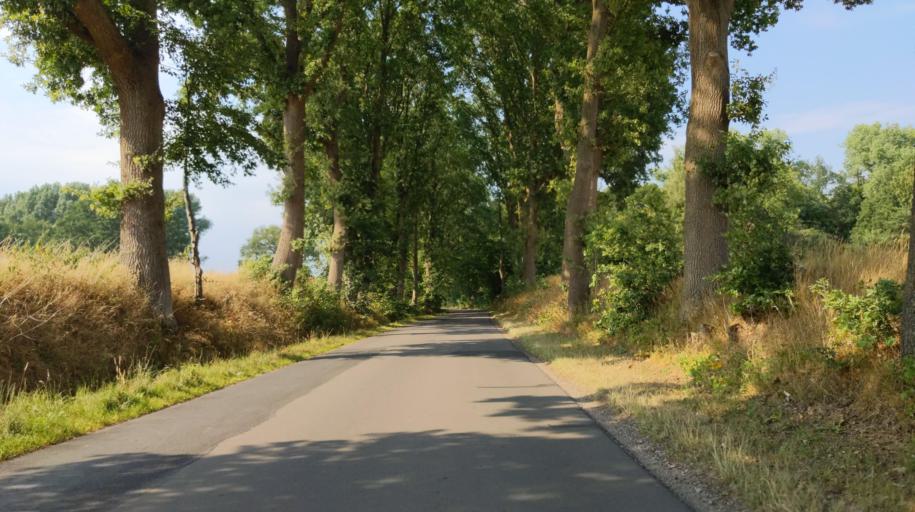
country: DE
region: Schleswig-Holstein
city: Rondeshagen
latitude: 53.7627
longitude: 10.6271
